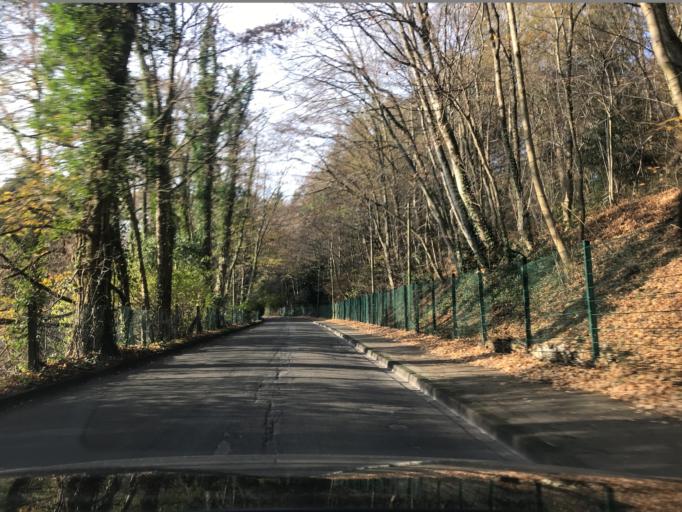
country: DE
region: North Rhine-Westphalia
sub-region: Regierungsbezirk Dusseldorf
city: Solingen
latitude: 51.1795
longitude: 7.0537
